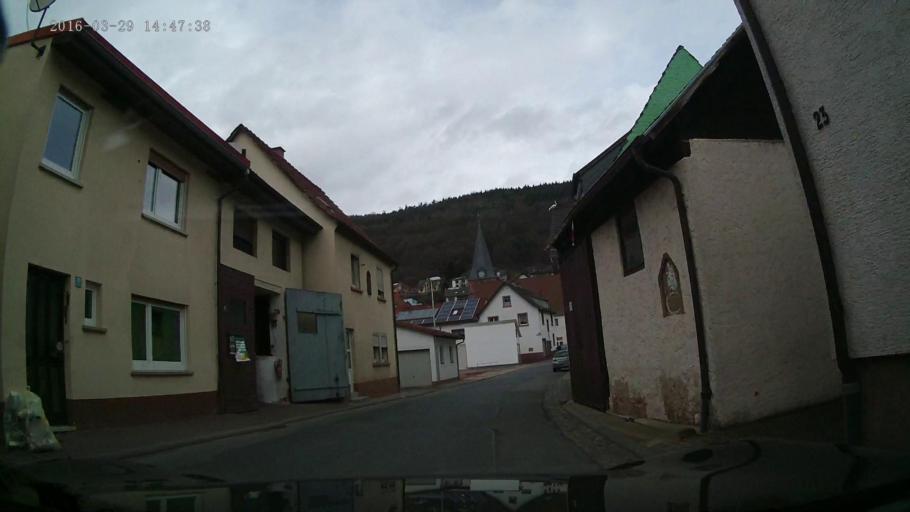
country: DE
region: Bavaria
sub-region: Regierungsbezirk Unterfranken
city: Weilbach
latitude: 49.6387
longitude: 9.2468
